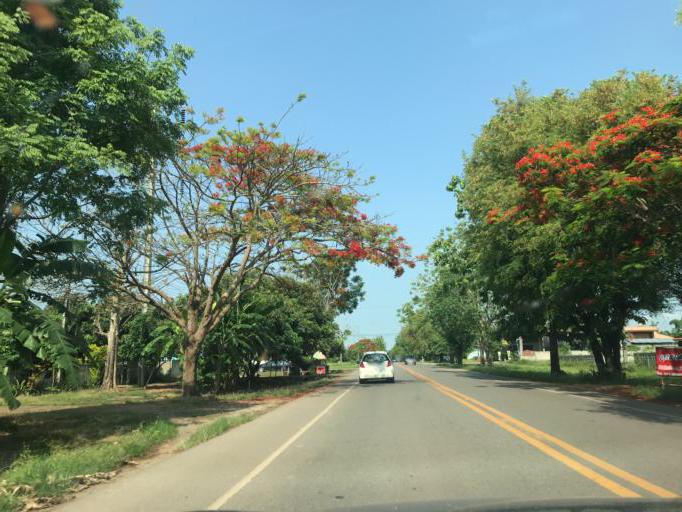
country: TH
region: Phayao
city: Chiang Kham
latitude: 19.4896
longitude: 100.2655
